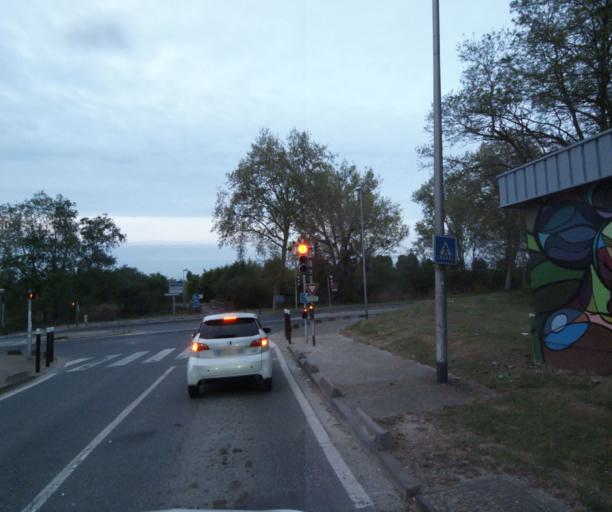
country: FR
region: Ile-de-France
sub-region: Departement de Seine-et-Marne
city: Torcy
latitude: 48.8592
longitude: 2.6557
